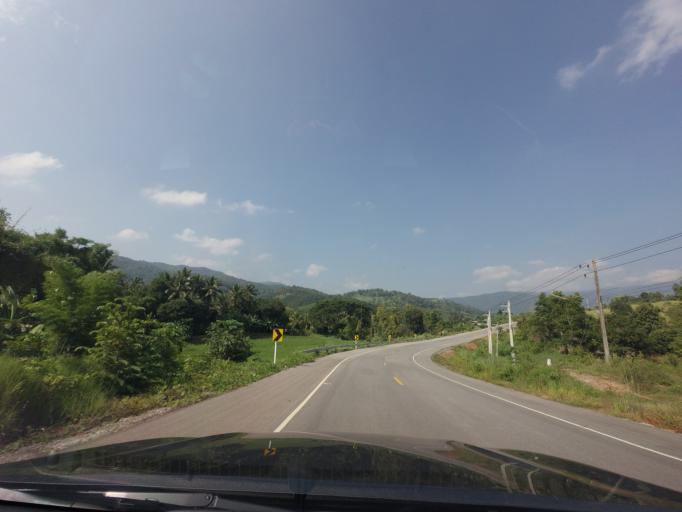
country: TH
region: Loei
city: Na Haeo
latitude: 17.4952
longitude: 101.0289
